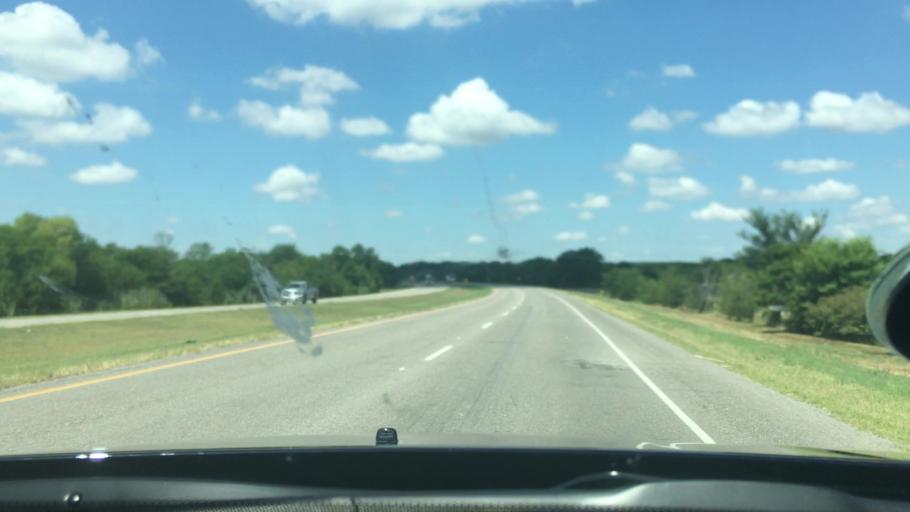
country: US
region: Oklahoma
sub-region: Carter County
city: Wilson
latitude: 34.1735
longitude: -97.3647
